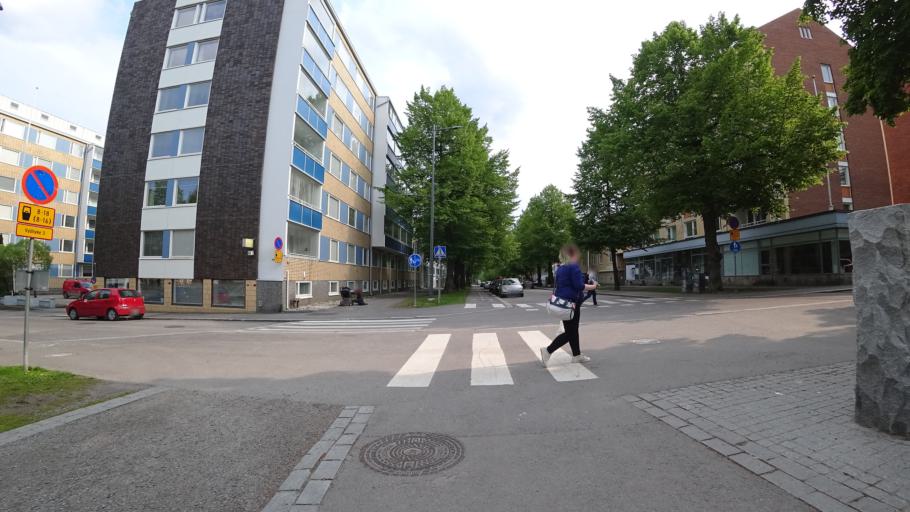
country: FI
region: Pirkanmaa
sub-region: Tampere
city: Tampere
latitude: 61.4960
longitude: 23.7476
